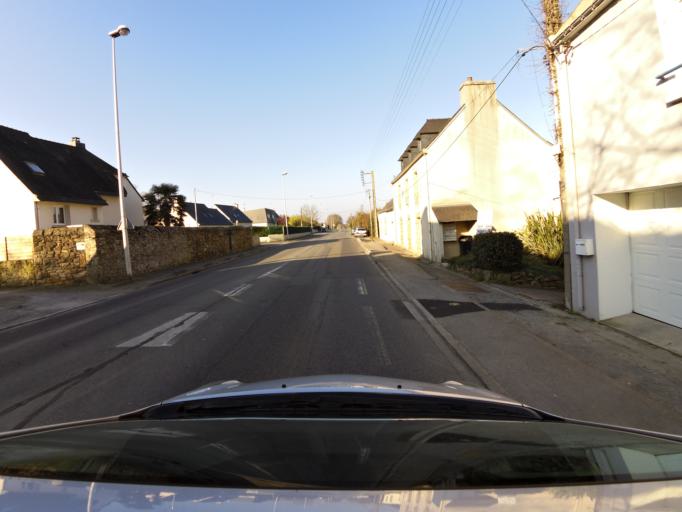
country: FR
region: Brittany
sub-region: Departement du Morbihan
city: Ploemeur
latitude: 47.7429
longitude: -3.4023
